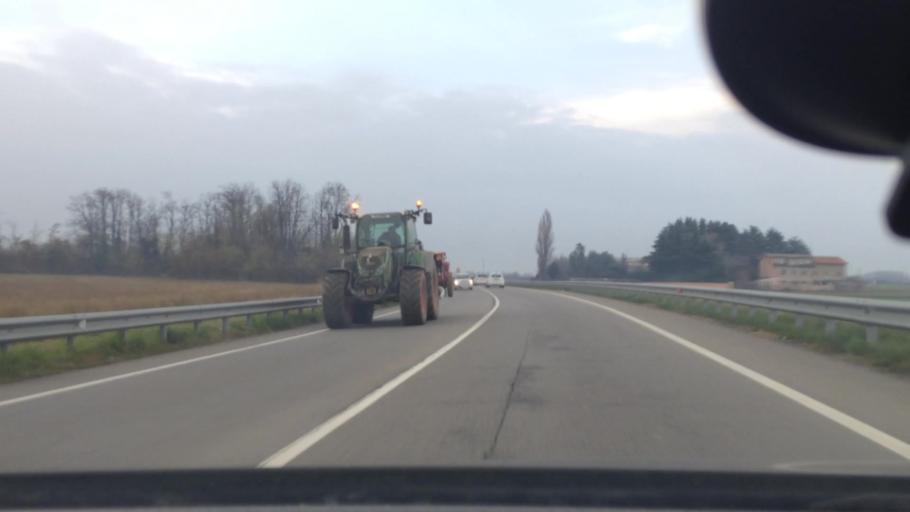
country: IT
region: Lombardy
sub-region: Provincia di Monza e Brianza
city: Ceriano Laghetto
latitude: 45.6259
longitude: 9.0600
